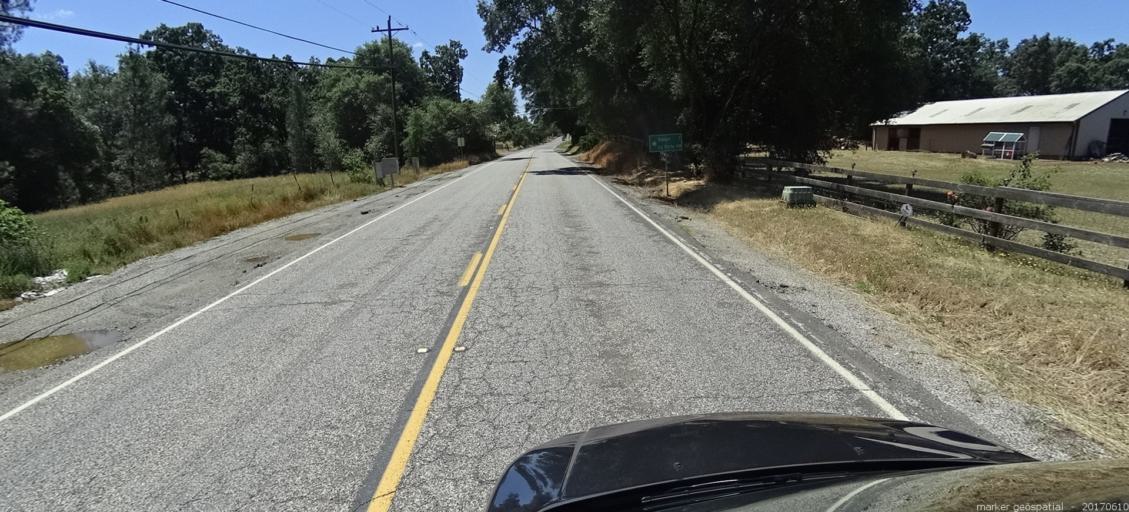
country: US
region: California
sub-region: Butte County
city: Oroville East
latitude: 39.4689
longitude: -121.4591
